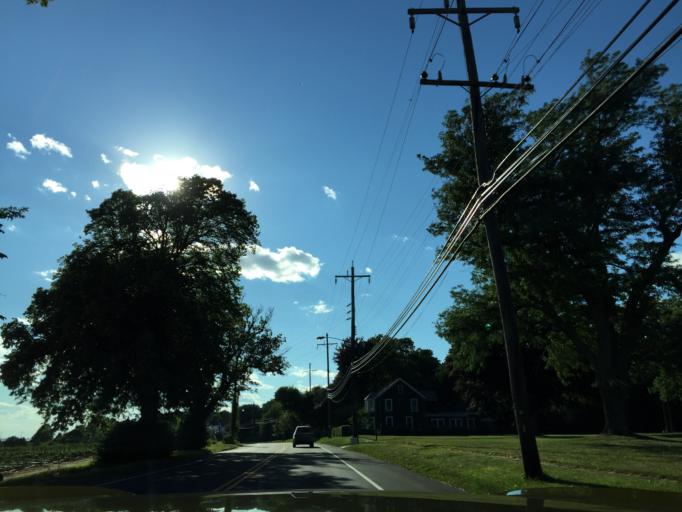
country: US
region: New York
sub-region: Suffolk County
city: Greenport
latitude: 41.1432
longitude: -72.3053
